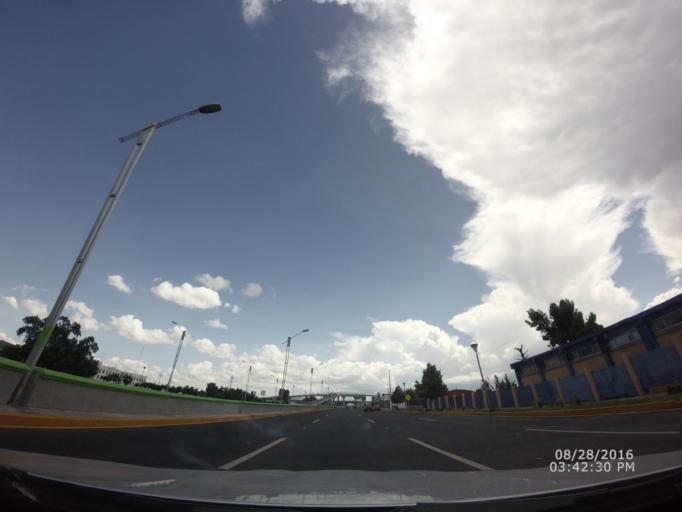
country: MX
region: Hidalgo
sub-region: Mineral de la Reforma
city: PRI Chacon
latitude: 20.0934
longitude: -98.7490
